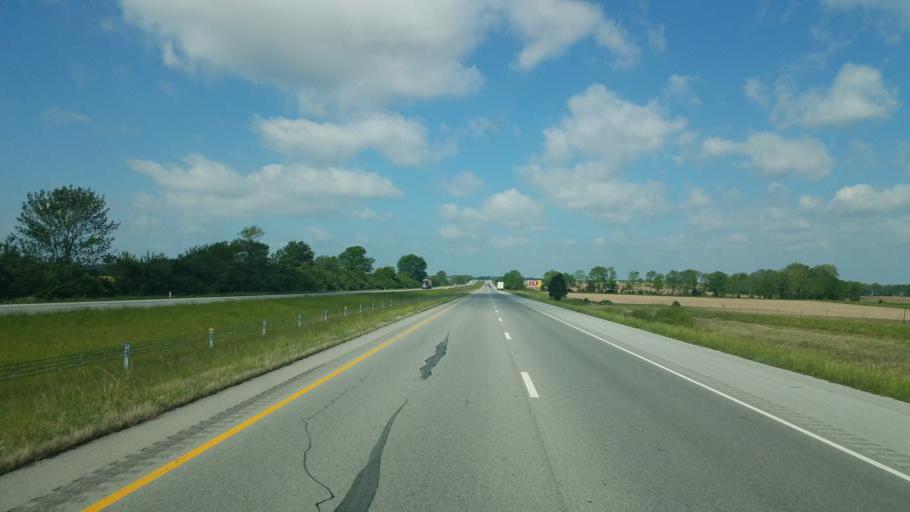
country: US
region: Indiana
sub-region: Putnam County
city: Cloverdale
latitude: 39.5568
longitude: -86.6793
